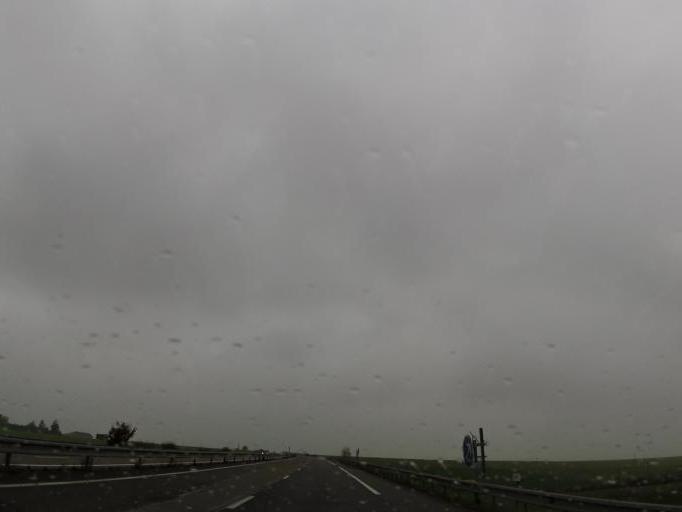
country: FR
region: Champagne-Ardenne
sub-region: Departement de la Marne
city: Sainte-Menehould
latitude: 49.0697
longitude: 4.7520
